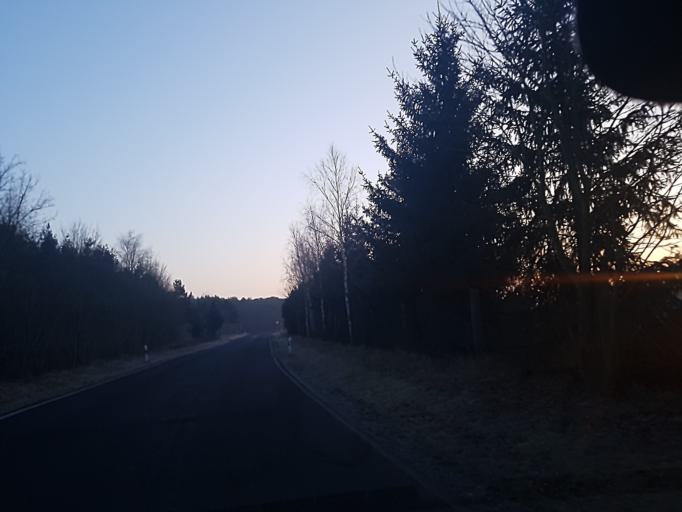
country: DE
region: Brandenburg
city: Herzberg
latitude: 51.7383
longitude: 13.2035
